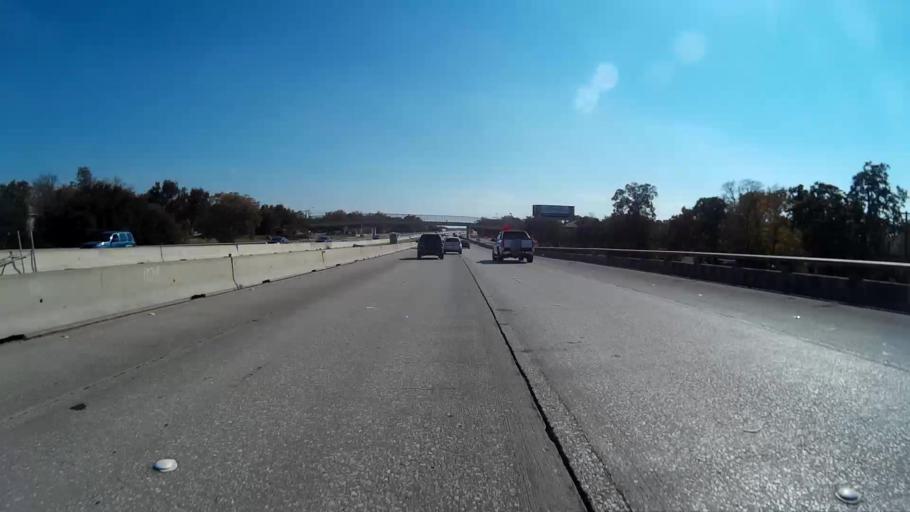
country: US
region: Texas
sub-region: Dallas County
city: Dallas
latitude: 32.7598
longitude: -96.7740
